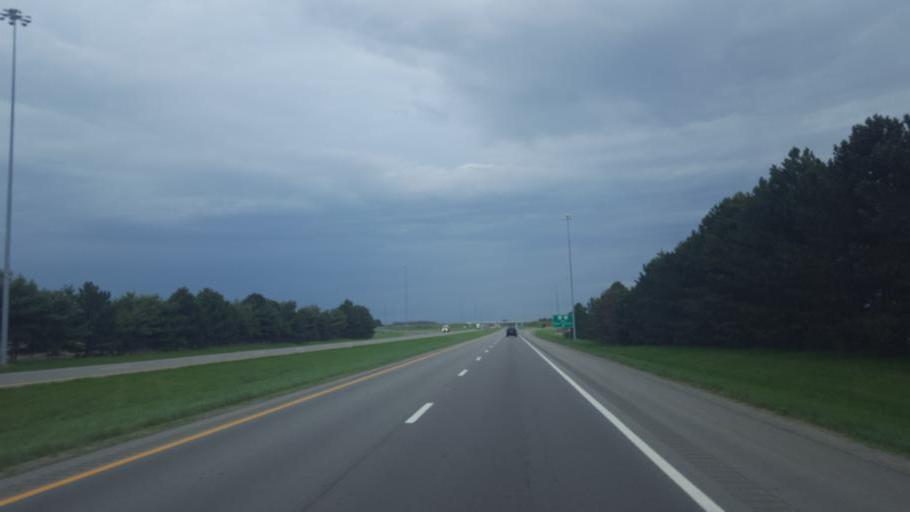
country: US
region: Ohio
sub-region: Wyandot County
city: Upper Sandusky
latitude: 40.8581
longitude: -83.2881
